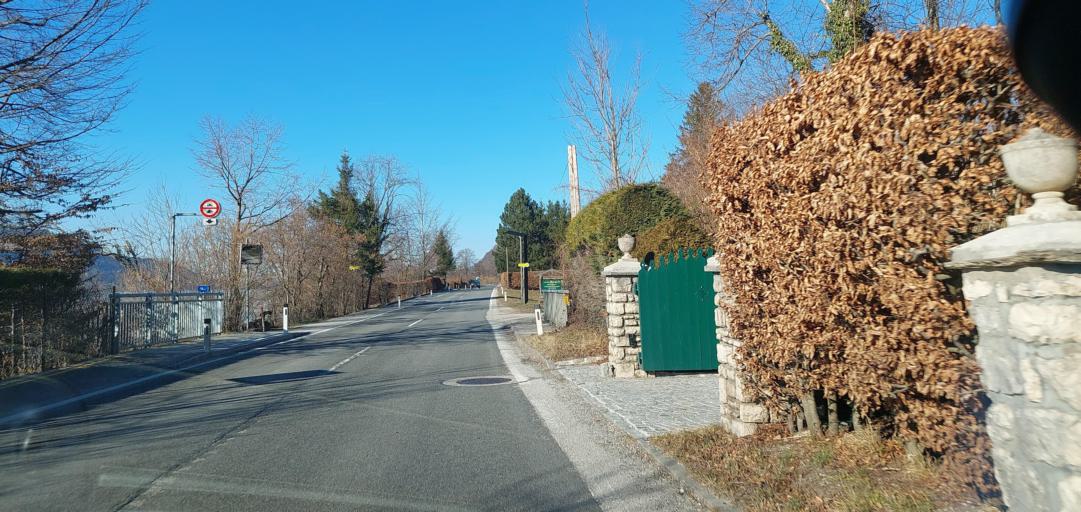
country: AT
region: Upper Austria
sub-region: Politischer Bezirk Vocklabruck
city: Steinbach am Attersee
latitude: 47.8182
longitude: 13.5473
